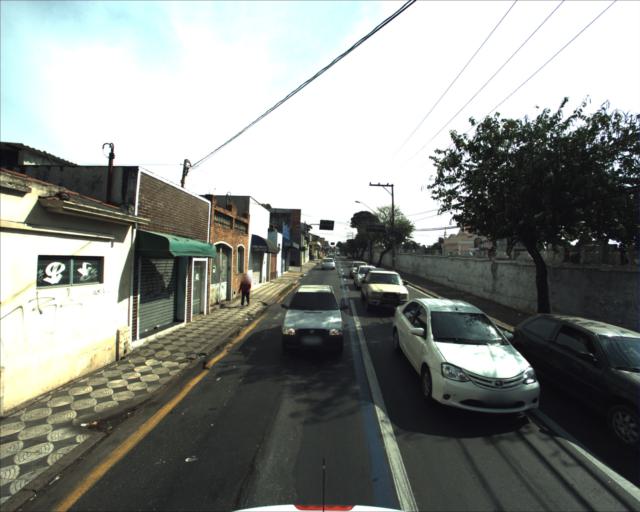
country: BR
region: Sao Paulo
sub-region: Sorocaba
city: Sorocaba
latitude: -23.4921
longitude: -47.4602
